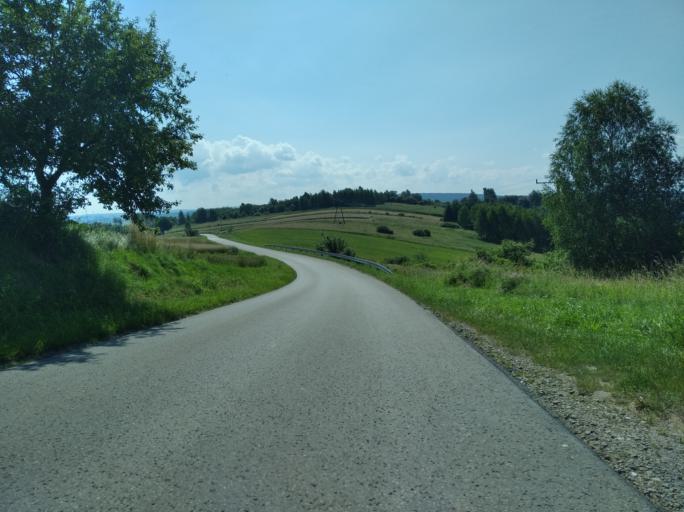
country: PL
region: Subcarpathian Voivodeship
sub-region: Powiat rzeszowski
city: Dynow
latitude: 49.8135
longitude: 22.2058
